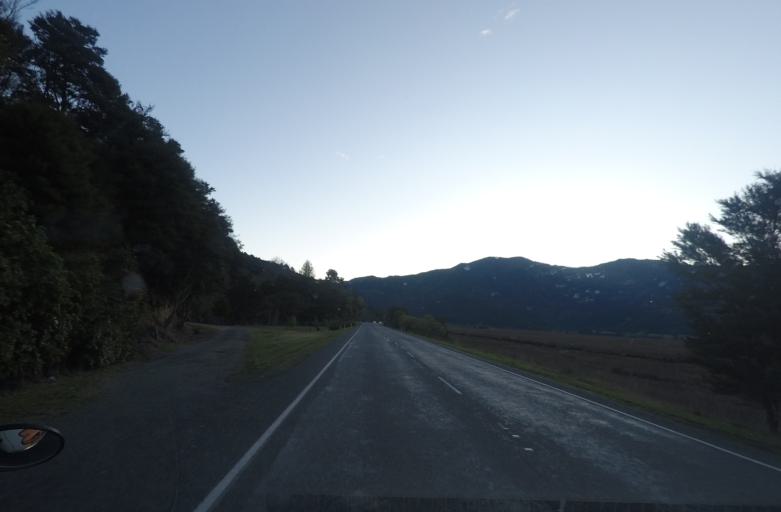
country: NZ
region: Marlborough
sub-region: Marlborough District
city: Picton
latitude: -41.2741
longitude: 173.7573
